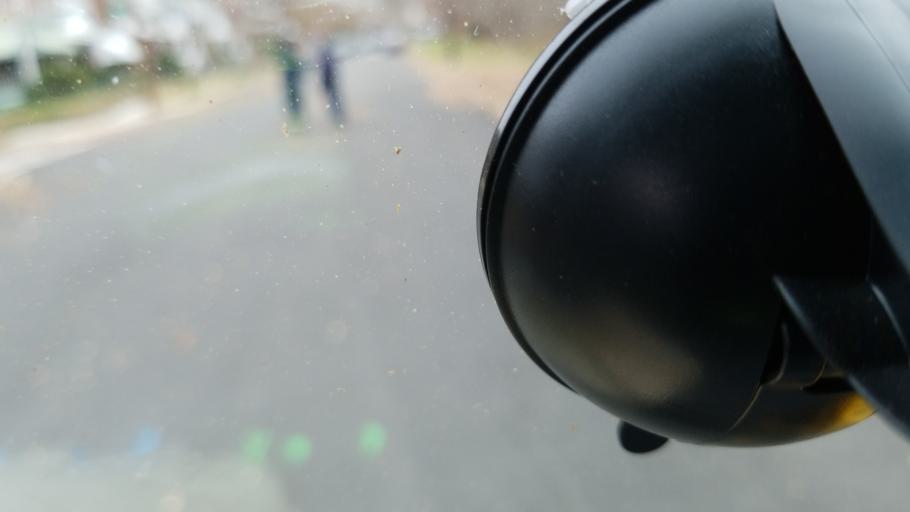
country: US
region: Maryland
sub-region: Prince George's County
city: Silver Hill
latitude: 38.8776
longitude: -76.9649
